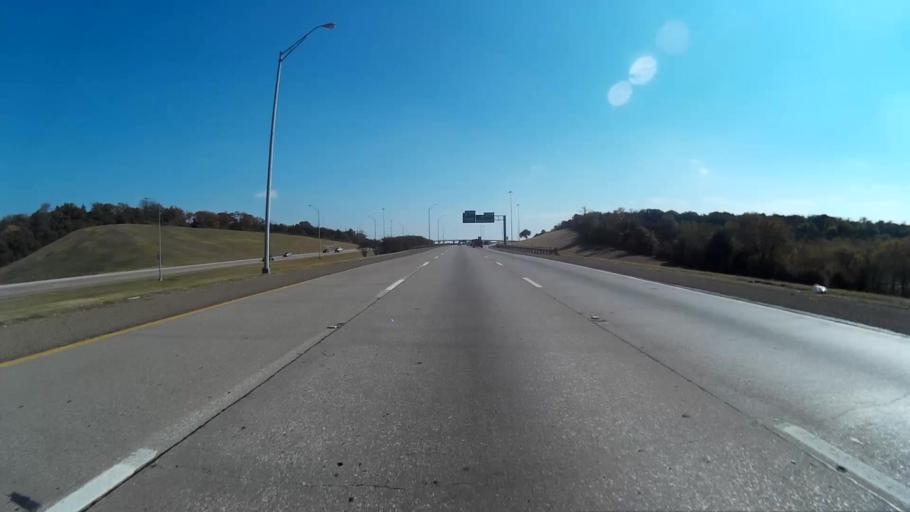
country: US
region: Texas
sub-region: Dallas County
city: Hutchins
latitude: 32.6682
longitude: -96.7329
